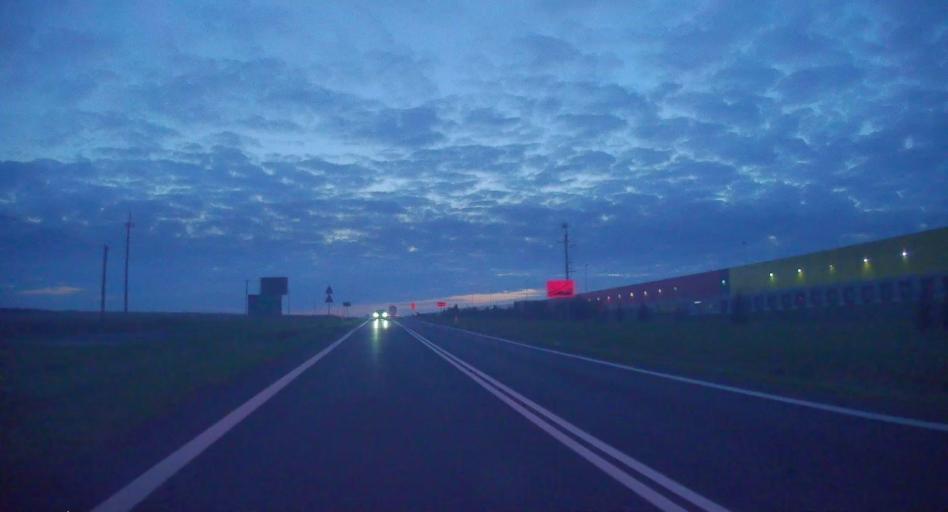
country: PL
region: Silesian Voivodeship
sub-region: Powiat klobucki
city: Lobodno
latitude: 50.8849
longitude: 18.9825
